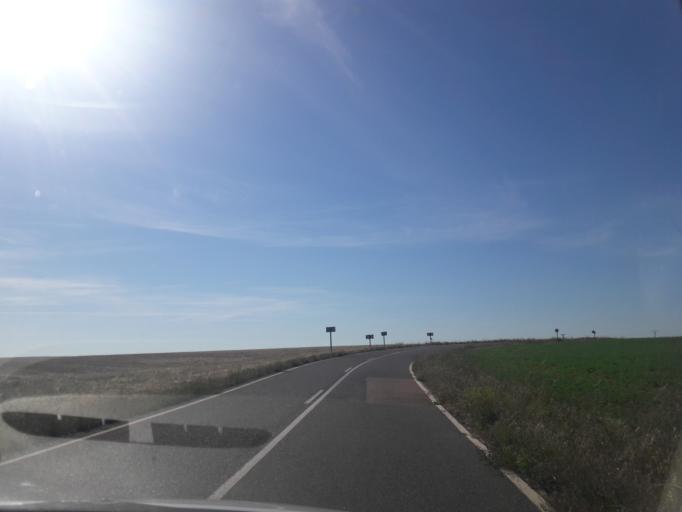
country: ES
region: Castille and Leon
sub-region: Provincia de Salamanca
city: Aldeanueva de Figueroa
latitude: 41.1394
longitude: -5.5064
